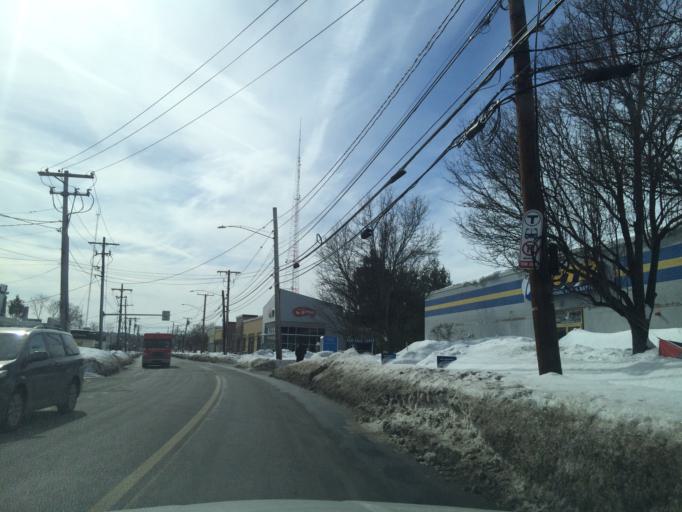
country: US
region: Massachusetts
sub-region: Middlesex County
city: Newton
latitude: 42.3162
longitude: -71.2098
